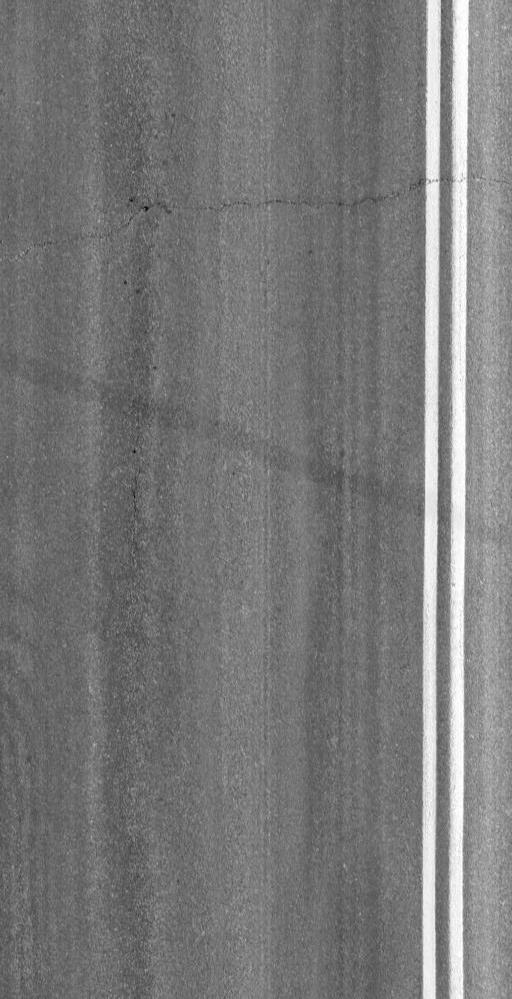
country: US
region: Vermont
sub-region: Chittenden County
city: Burlington
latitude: 44.3621
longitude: -73.2225
